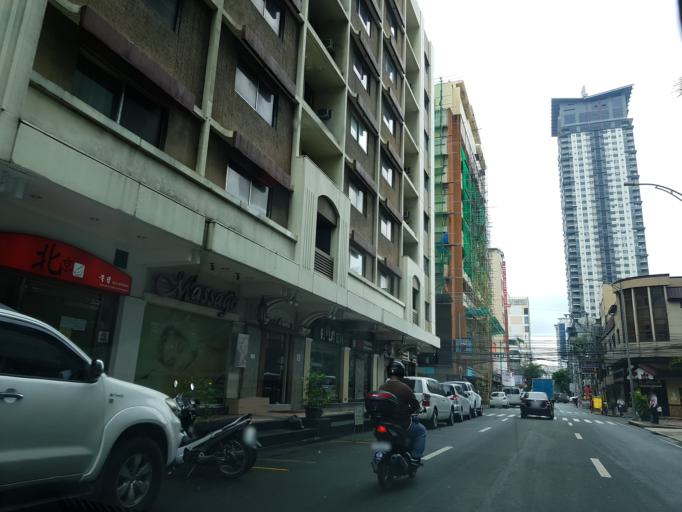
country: PH
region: Metro Manila
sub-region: City of Manila
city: Port Area
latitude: 14.5729
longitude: 120.9846
